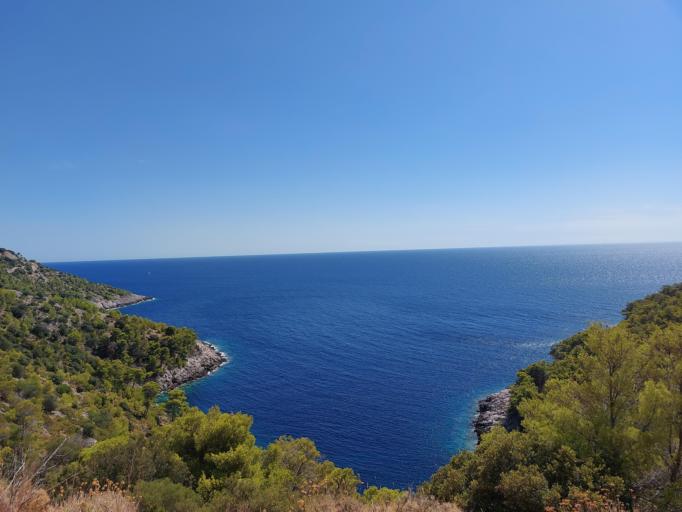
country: HR
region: Dubrovacko-Neretvanska
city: Smokvica
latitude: 42.7347
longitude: 16.8355
